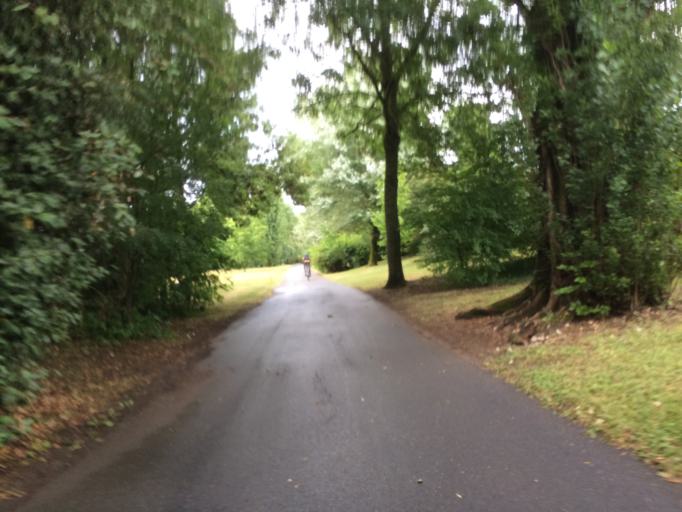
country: FR
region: Picardie
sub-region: Departement de l'Oise
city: Venette
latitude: 49.4032
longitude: 2.7958
